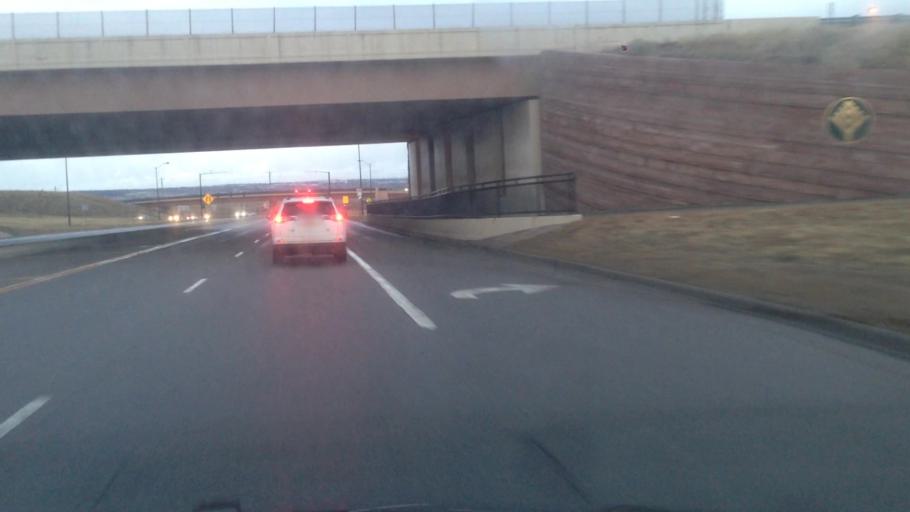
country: US
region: Colorado
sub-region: Douglas County
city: Meridian
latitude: 39.5239
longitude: -104.8681
